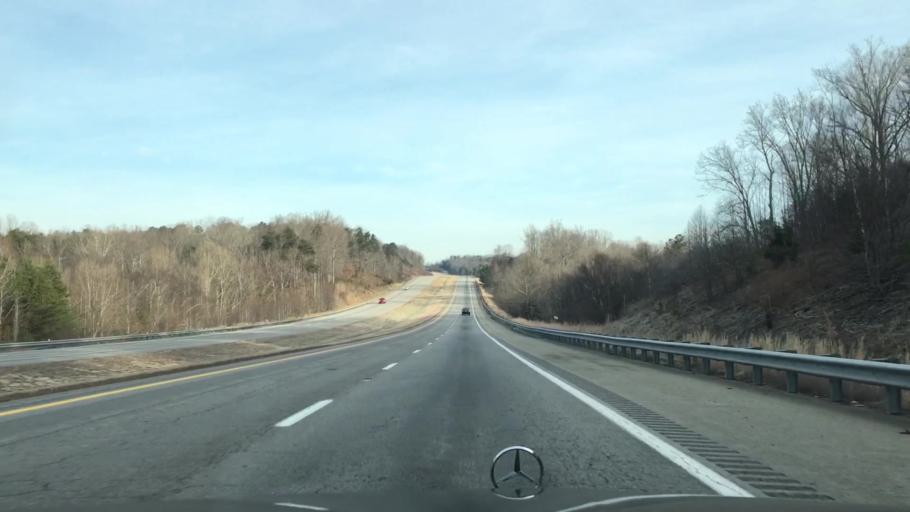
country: US
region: Virginia
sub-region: City of Danville
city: Danville
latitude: 36.6429
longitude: -79.3644
